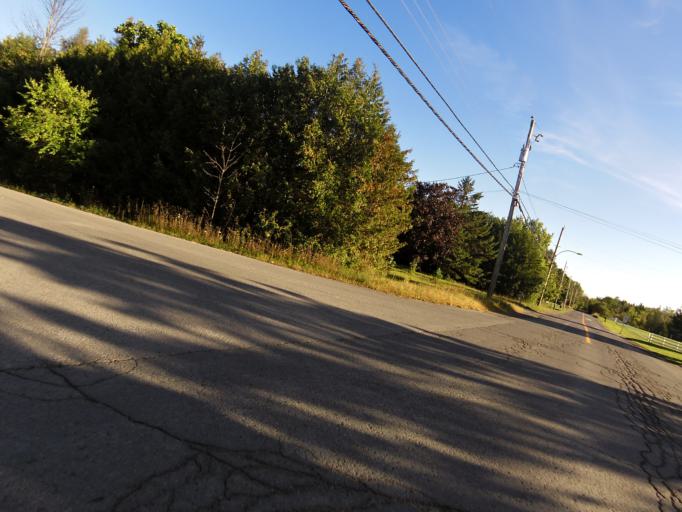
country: CA
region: Ontario
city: Bells Corners
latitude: 45.4278
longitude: -75.8790
